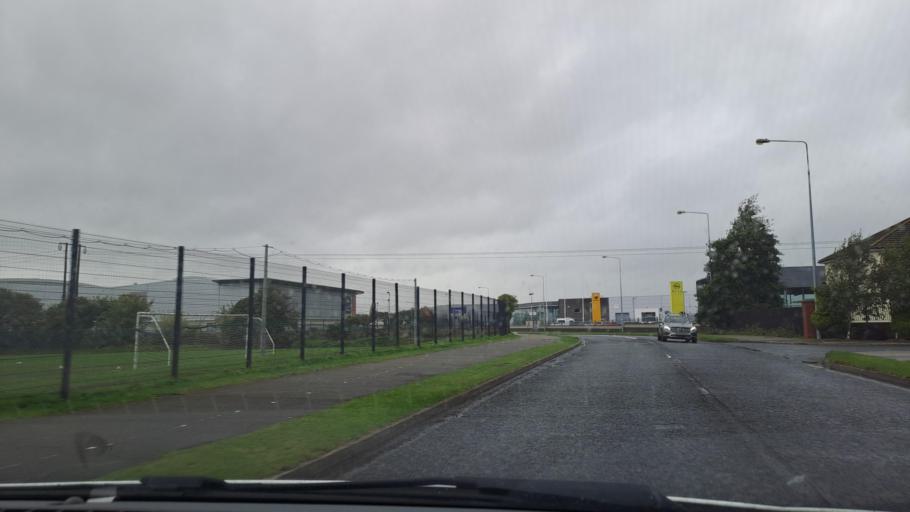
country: IE
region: Leinster
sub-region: Lu
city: Blackrock
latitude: 53.9883
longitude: -6.3724
